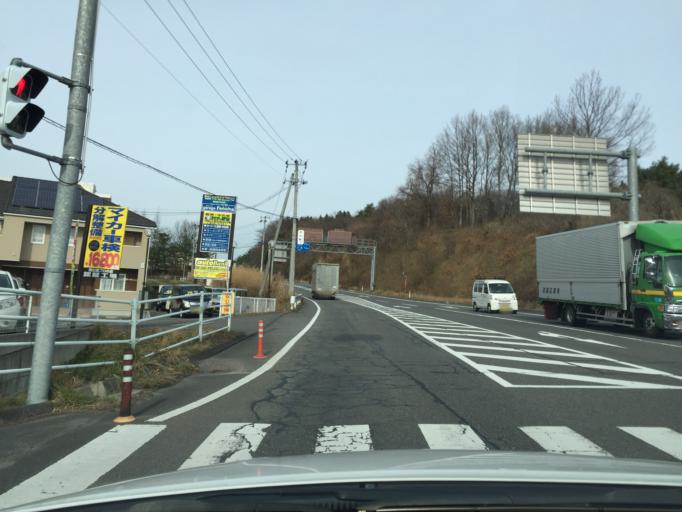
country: JP
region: Fukushima
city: Funehikimachi-funehiki
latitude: 37.2922
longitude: 140.6174
